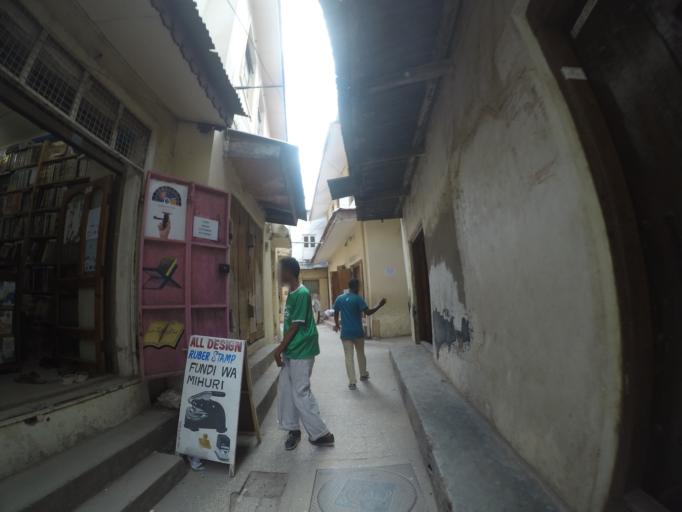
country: TZ
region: Zanzibar Urban/West
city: Zanzibar
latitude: -6.1627
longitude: 39.1920
